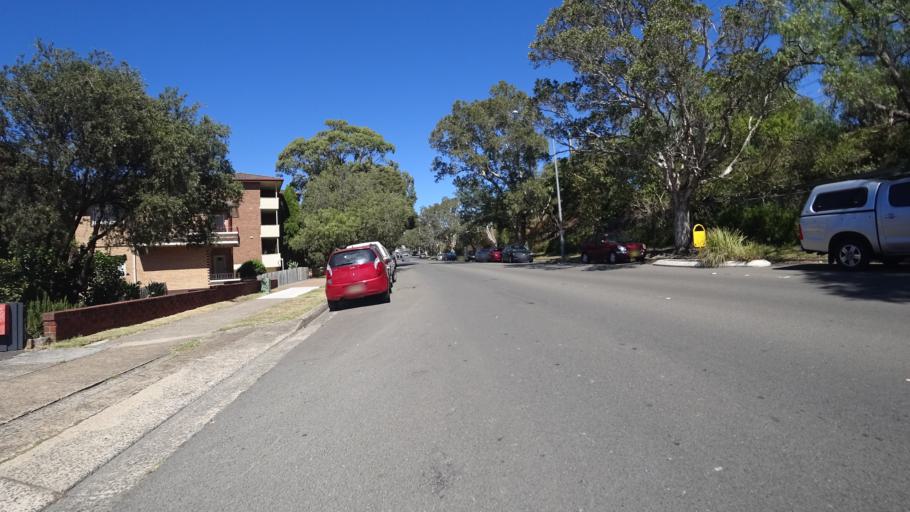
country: AU
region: New South Wales
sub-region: Kogarah
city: Kogarah Bay
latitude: -33.9690
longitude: 151.1221
